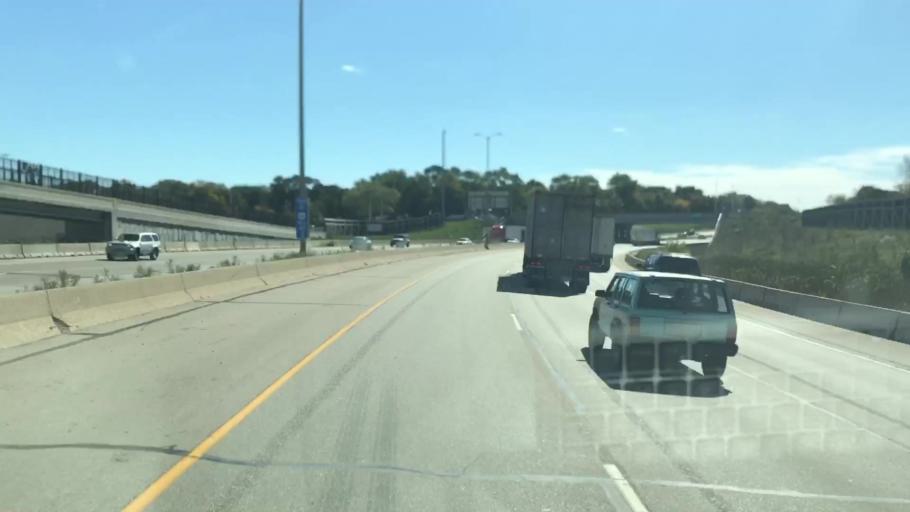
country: US
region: Wisconsin
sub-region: Waukesha County
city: Elm Grove
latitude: 43.0694
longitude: -88.0543
